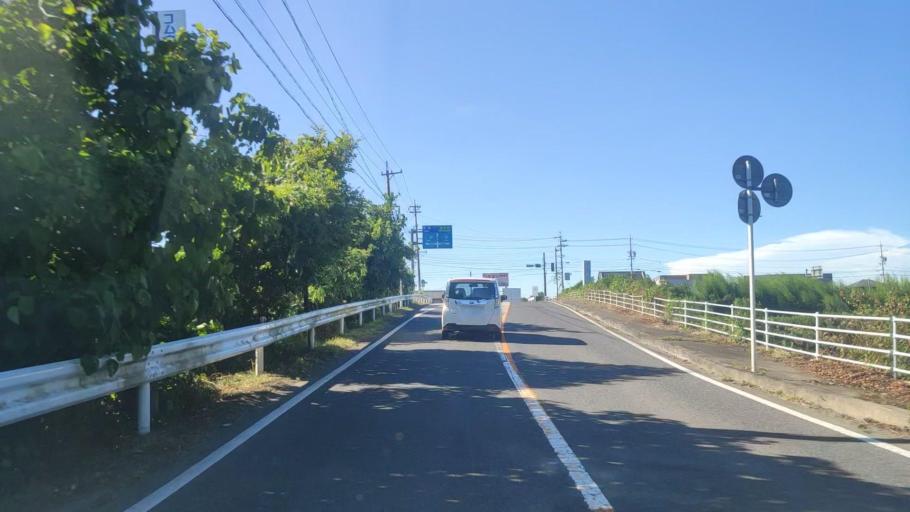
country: JP
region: Mie
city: Ueno-ebisumachi
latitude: 34.8357
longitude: 136.2358
